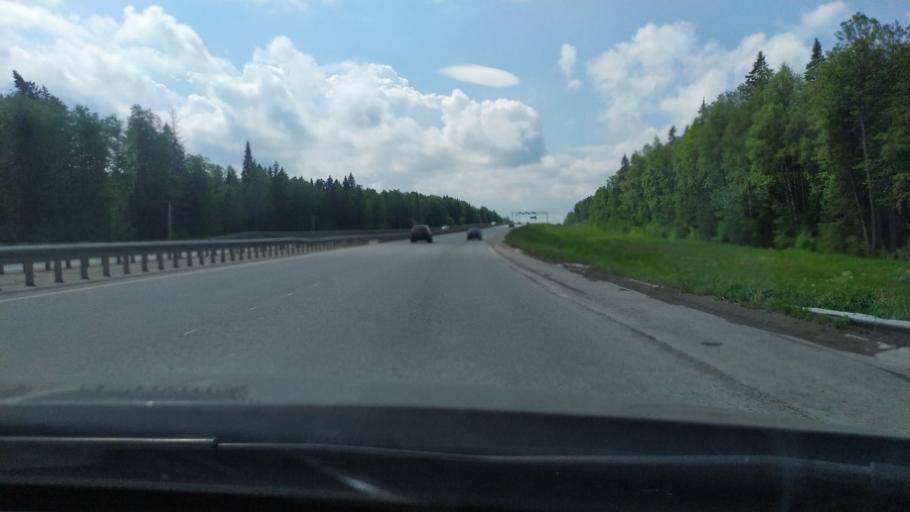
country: RU
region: Perm
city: Ferma
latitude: 58.0299
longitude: 56.4319
